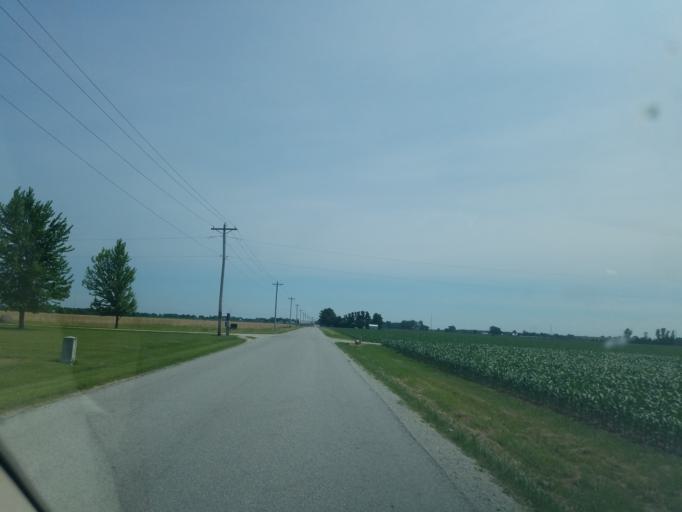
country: US
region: Ohio
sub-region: Seneca County
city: Tiffin
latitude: 41.1346
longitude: -83.2376
